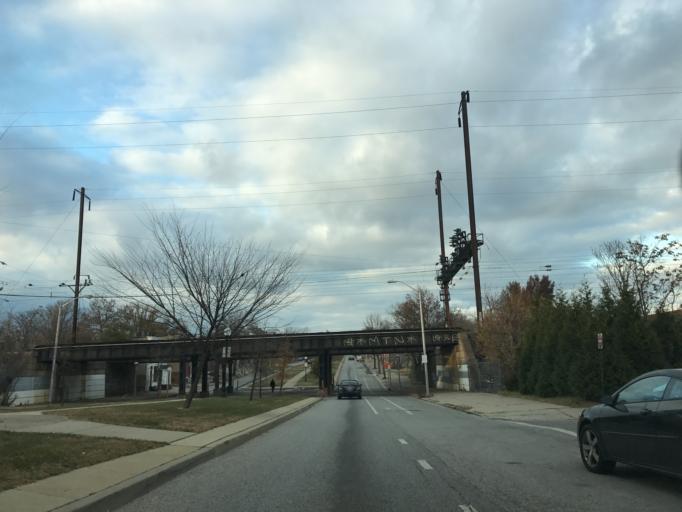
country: US
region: Maryland
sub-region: City of Baltimore
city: Baltimore
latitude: 39.3057
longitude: -76.5946
